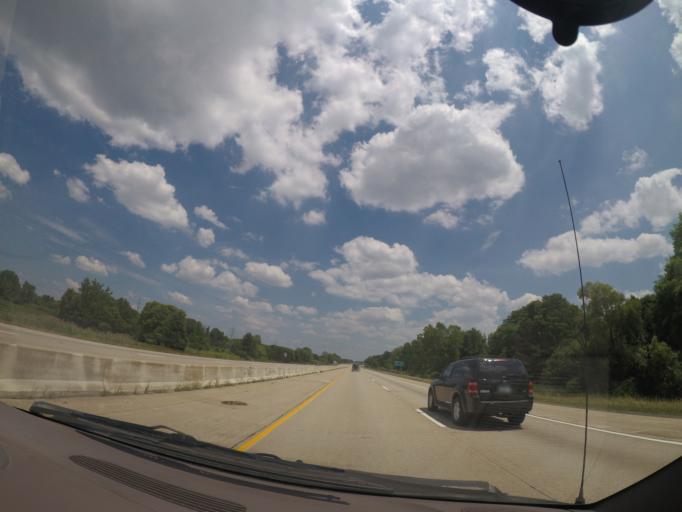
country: US
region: Indiana
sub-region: Saint Joseph County
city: Mishawaka
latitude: 41.6244
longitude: -86.1910
